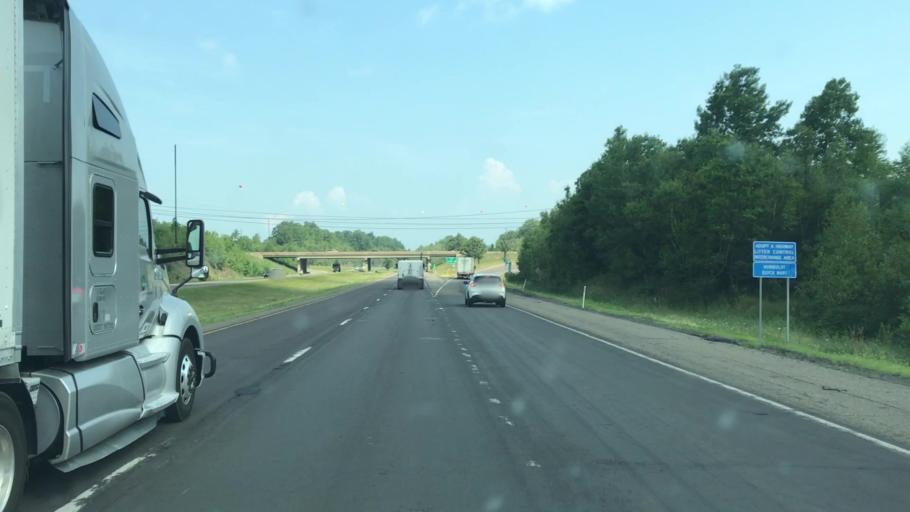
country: US
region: Pennsylvania
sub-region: Luzerne County
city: West Hazleton
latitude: 40.9399
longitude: -76.0233
